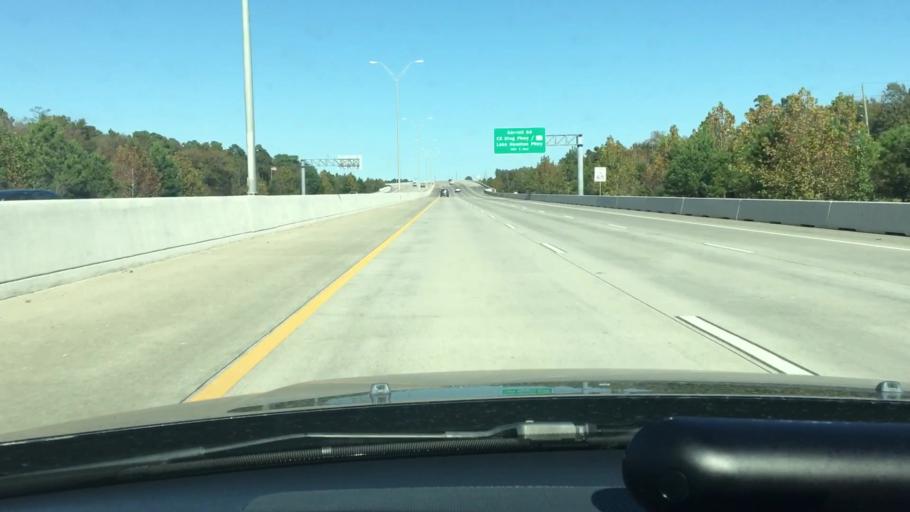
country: US
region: Texas
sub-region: Harris County
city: Sheldon
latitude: 29.8648
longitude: -95.1872
